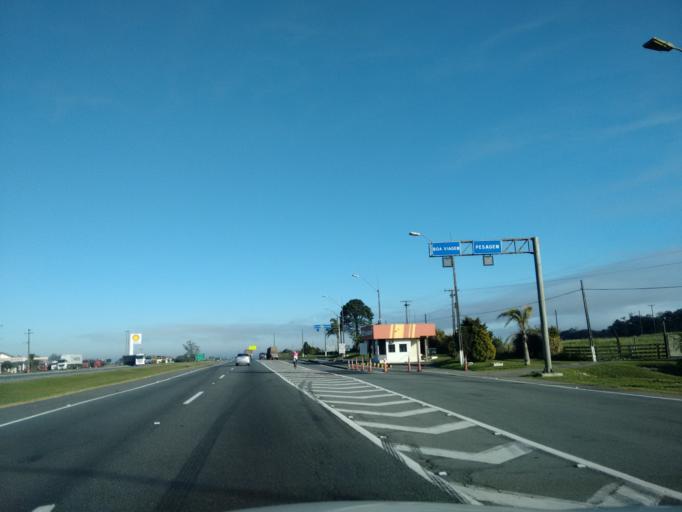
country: BR
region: Parana
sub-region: Campo Largo
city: Campo Largo
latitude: -25.4716
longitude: -49.6662
